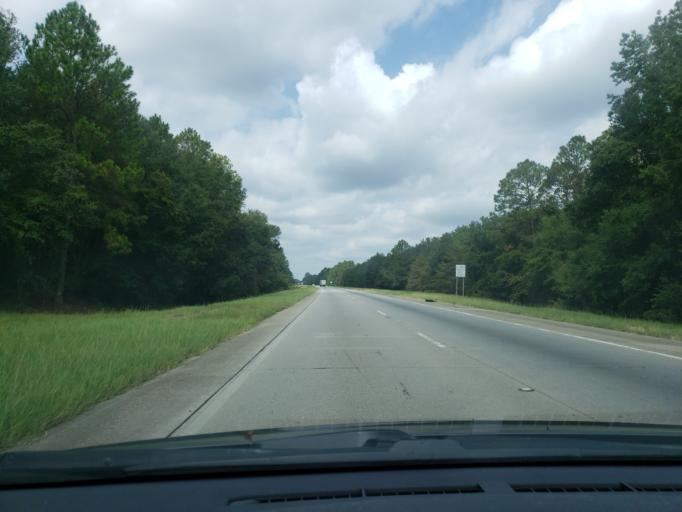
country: US
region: Georgia
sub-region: Treutlen County
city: Soperton
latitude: 32.4231
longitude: -82.4221
